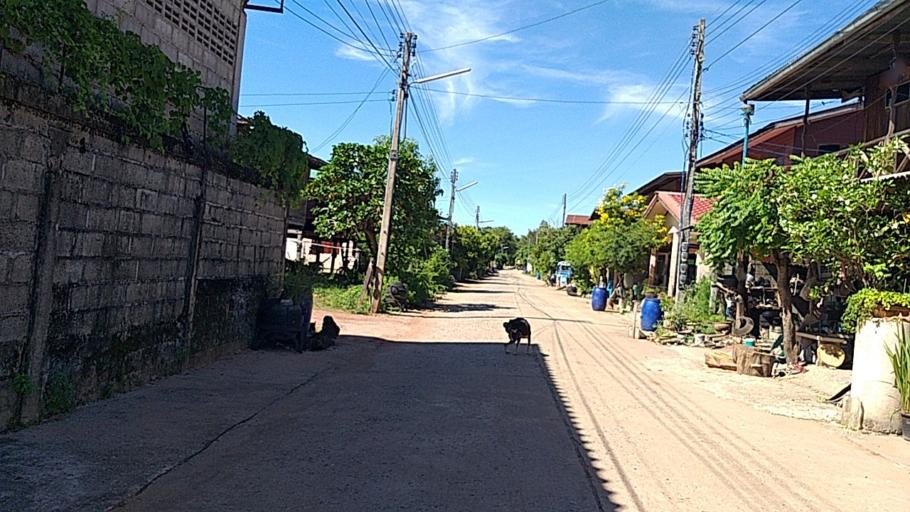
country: TH
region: Chaiyaphum
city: Ban Thaen
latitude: 16.4088
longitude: 102.3541
